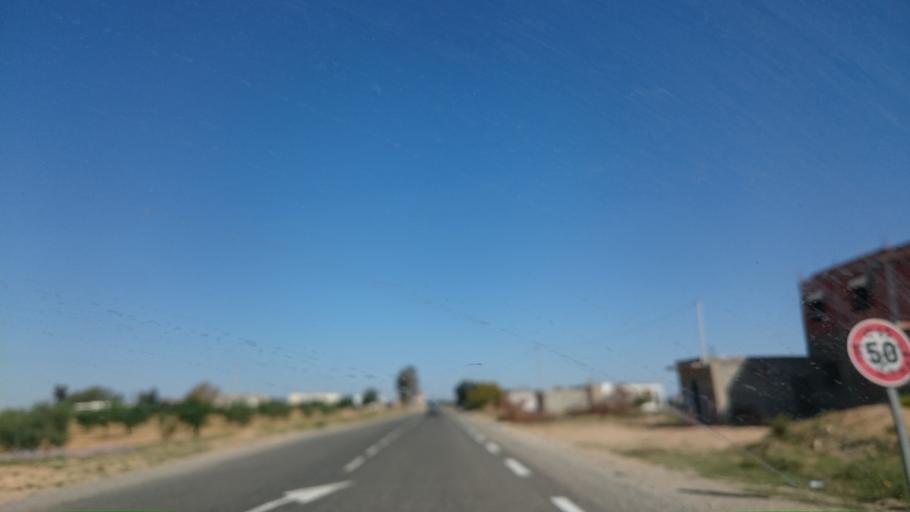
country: TN
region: Safaqis
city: Sfax
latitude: 34.7680
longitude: 10.5103
